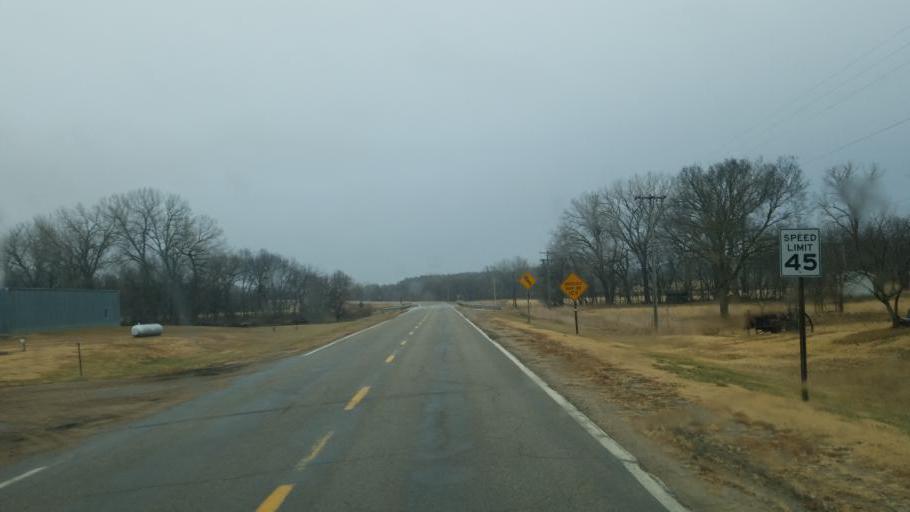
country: US
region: Nebraska
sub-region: Knox County
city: Center
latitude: 42.6076
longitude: -97.8768
